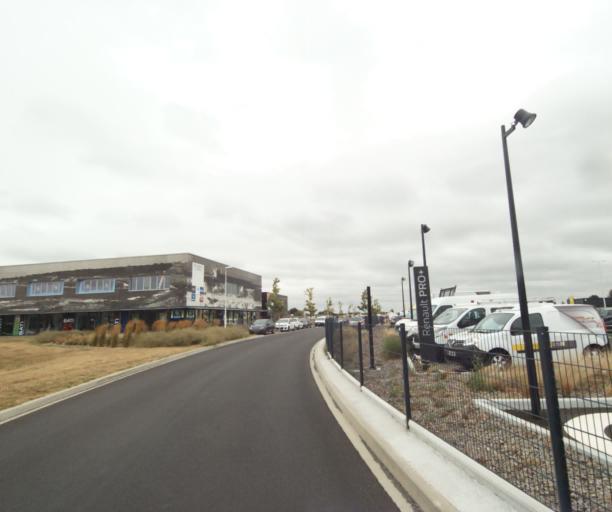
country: FR
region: Pays de la Loire
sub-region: Departement de la Vendee
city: Chateau-d'Olonne
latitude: 46.4971
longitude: -1.7534
